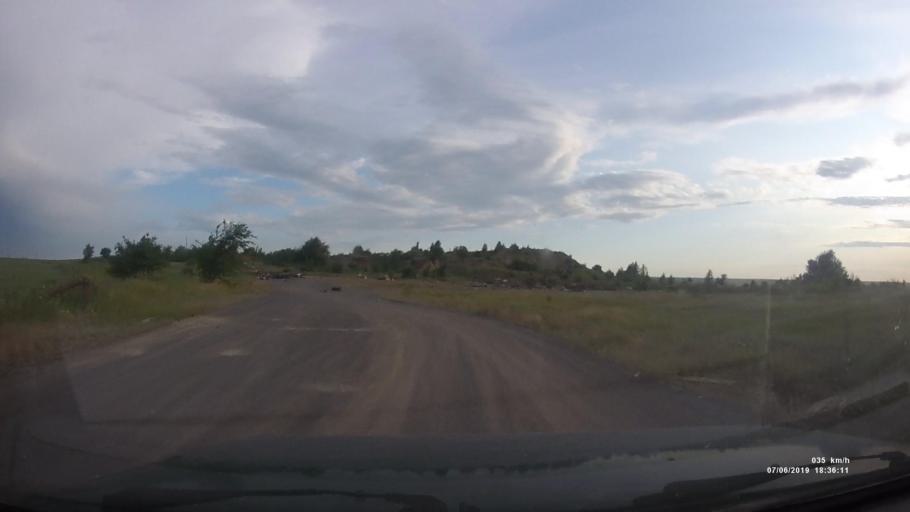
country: RU
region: Rostov
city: Staraya Stanitsa
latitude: 48.2527
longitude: 40.3547
